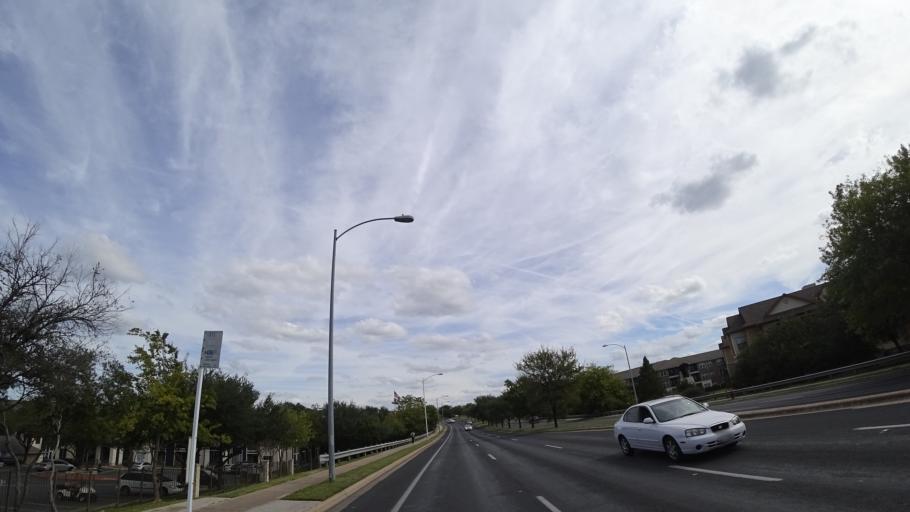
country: US
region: Texas
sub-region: Travis County
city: Onion Creek
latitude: 30.2023
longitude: -97.7709
